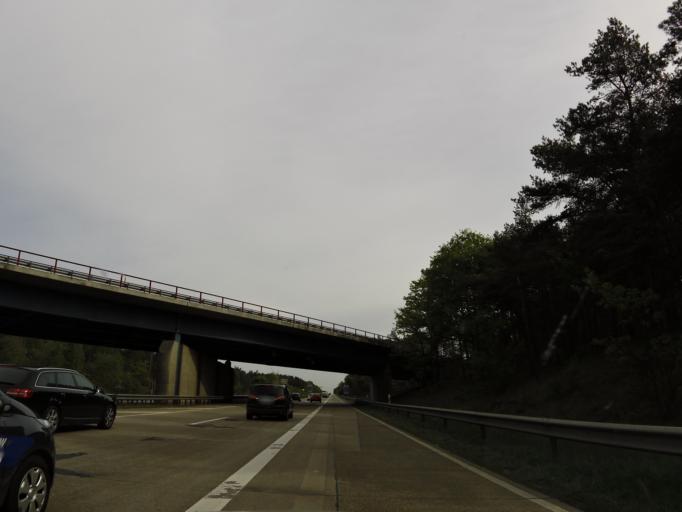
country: DE
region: Lower Saxony
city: Bad Fallingbostel
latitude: 52.7887
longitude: 9.6728
